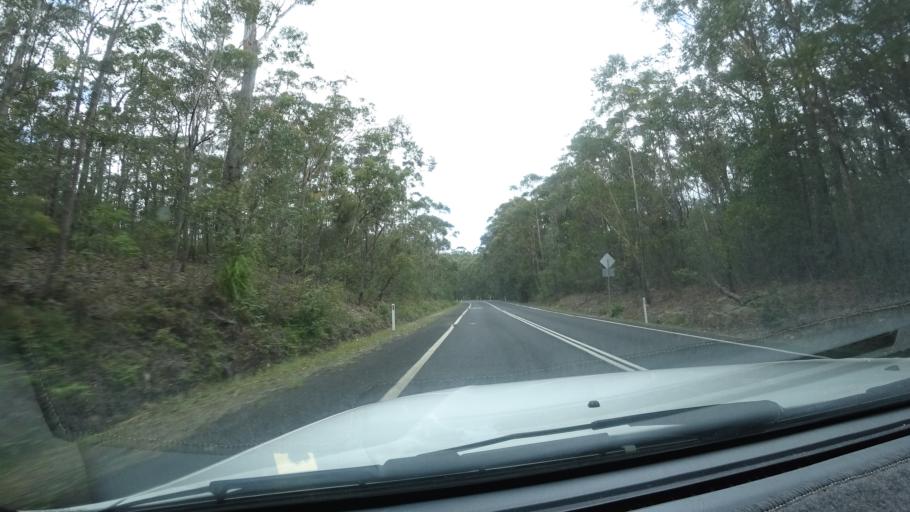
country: AU
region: New South Wales
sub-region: Shoalhaven Shire
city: Milton
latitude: -35.1956
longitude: 150.4442
